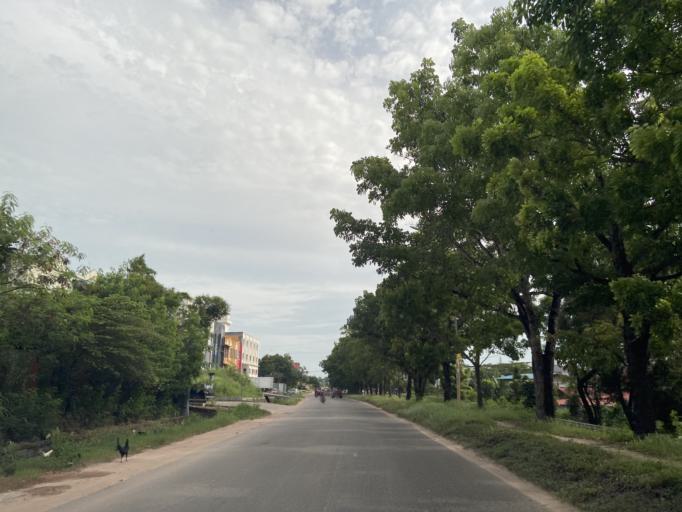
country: SG
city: Singapore
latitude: 1.1362
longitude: 104.0021
